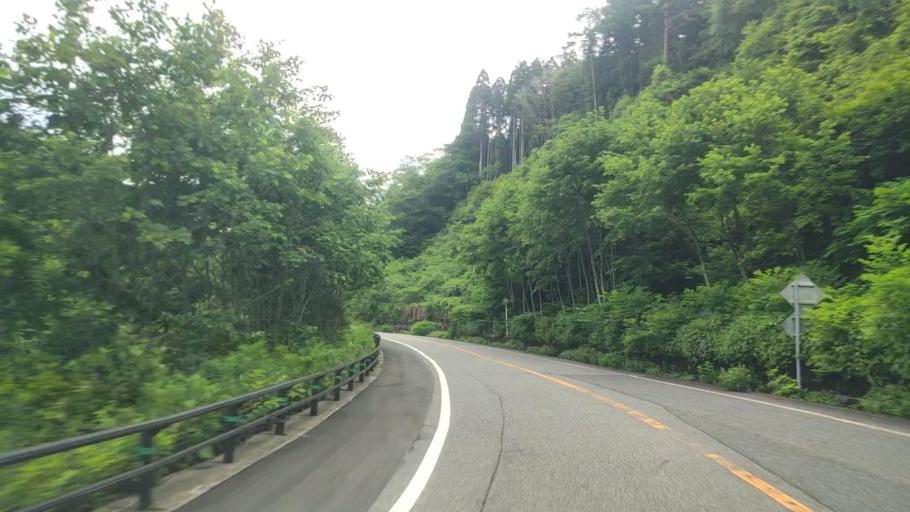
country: JP
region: Tottori
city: Yonago
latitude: 35.3368
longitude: 133.5582
